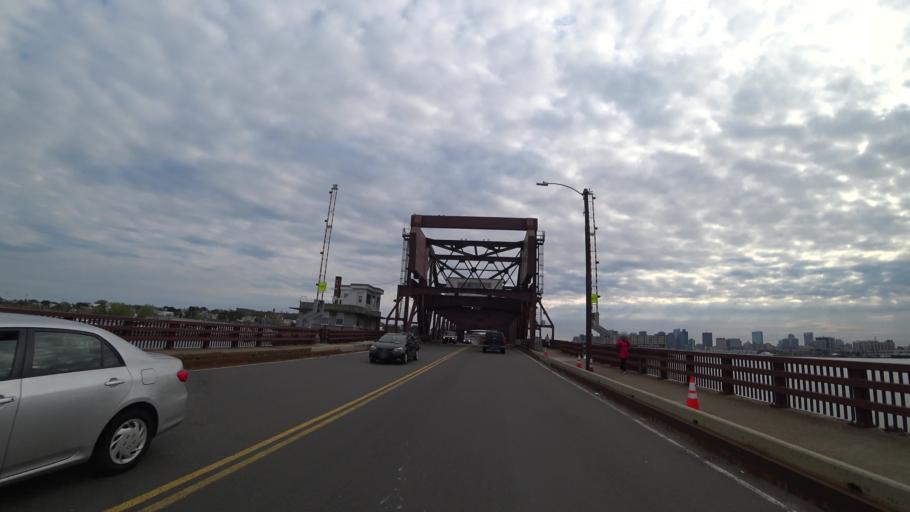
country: US
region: Massachusetts
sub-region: Suffolk County
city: Chelsea
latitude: 42.3865
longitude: -71.0394
